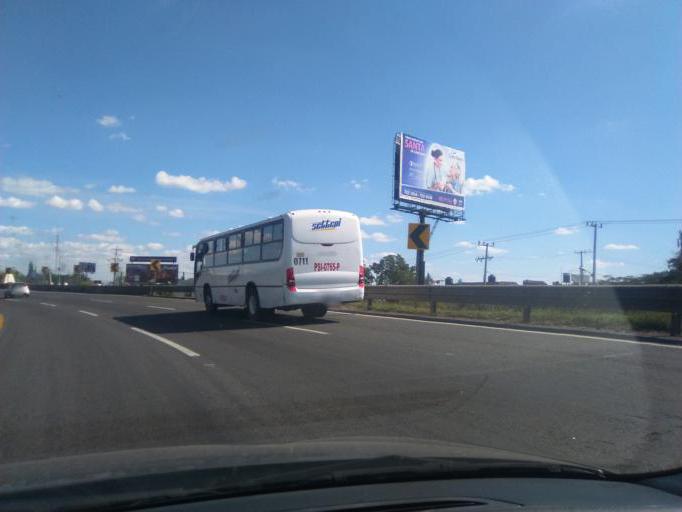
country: MX
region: Guanajuato
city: Silao
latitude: 20.9550
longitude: -101.4402
